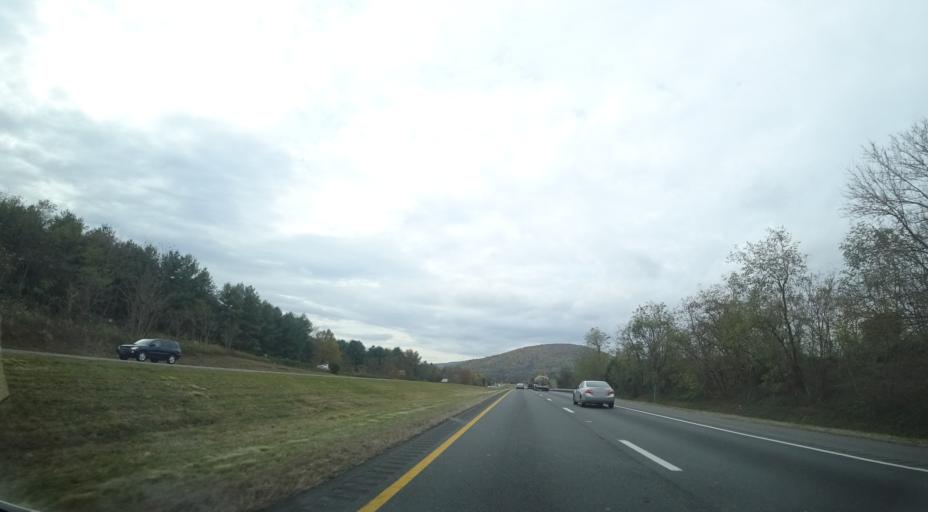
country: US
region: Virginia
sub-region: Fauquier County
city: Marshall
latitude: 38.9060
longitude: -77.9517
